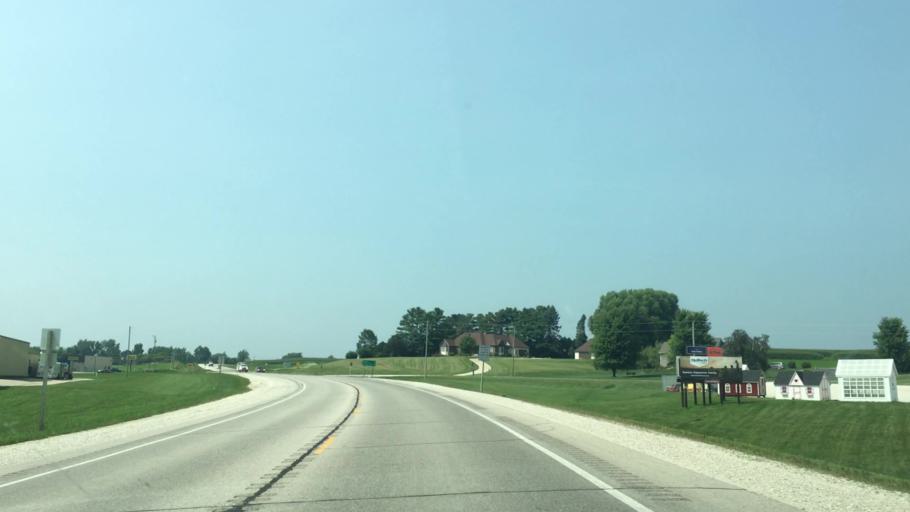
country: US
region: Iowa
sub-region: Winneshiek County
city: Decorah
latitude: 43.1894
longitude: -91.8652
